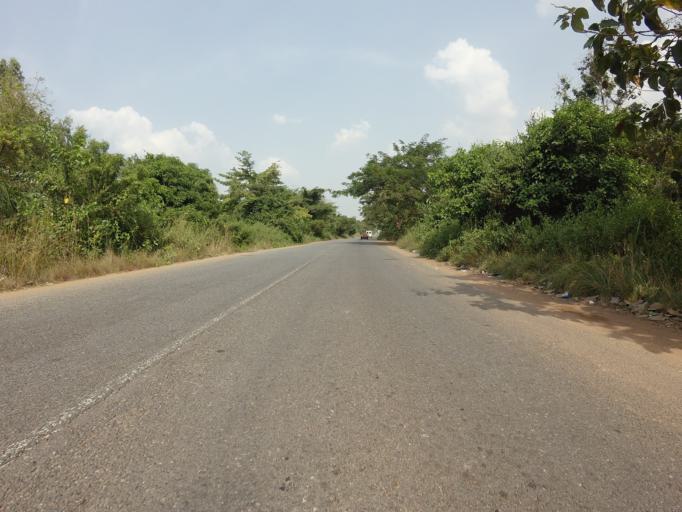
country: GH
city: Akropong
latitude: 5.9279
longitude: -0.0439
